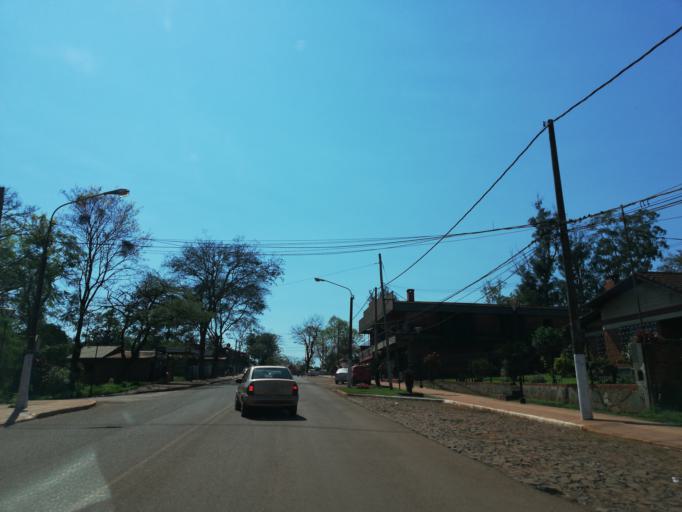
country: AR
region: Misiones
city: Puerto Eldorado
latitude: -26.4075
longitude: -54.6691
